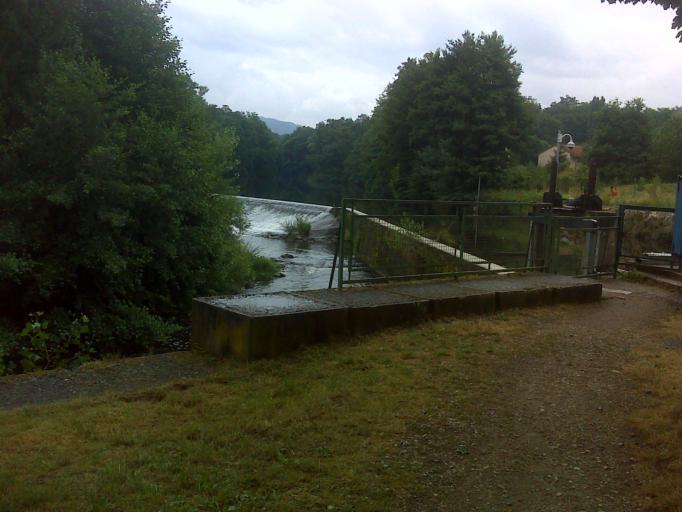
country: FR
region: Auvergne
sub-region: Departement de la Haute-Loire
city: Langeac
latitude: 45.0939
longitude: 3.5037
